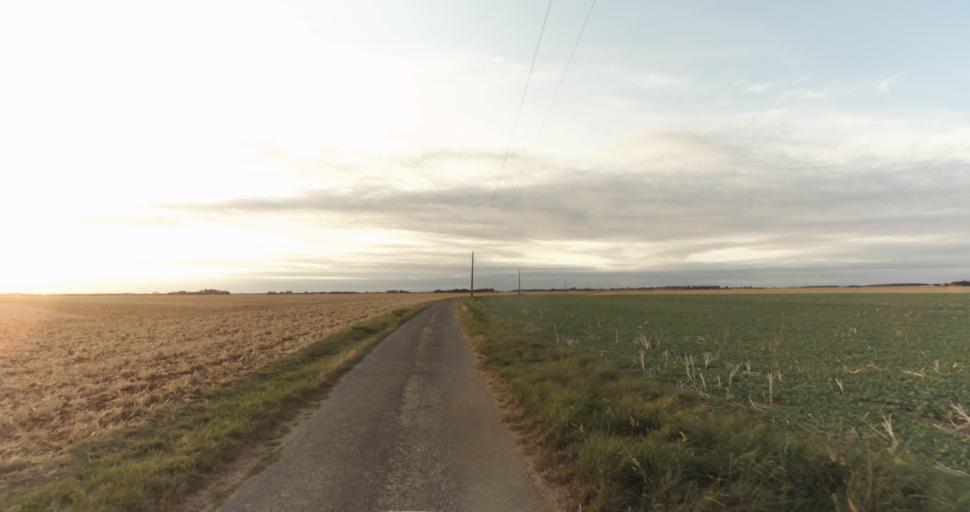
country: FR
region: Haute-Normandie
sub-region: Departement de l'Eure
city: La Madeleine-de-Nonancourt
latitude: 48.8581
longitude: 1.2102
